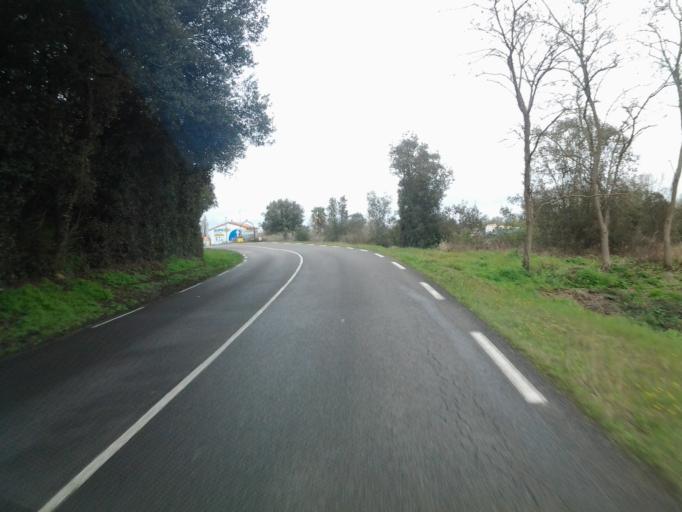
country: FR
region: Pays de la Loire
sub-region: Departement de la Vendee
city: Longeville-sur-Mer
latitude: 46.3834
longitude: -1.4658
